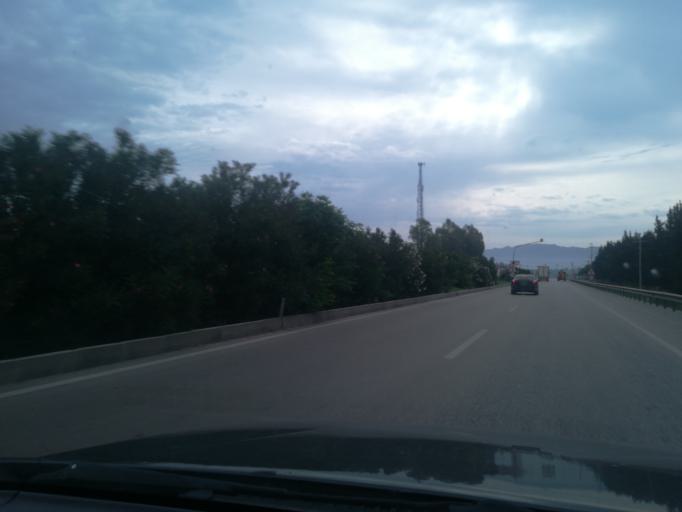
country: TR
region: Adana
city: Yakapinar
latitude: 36.9656
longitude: 35.6063
